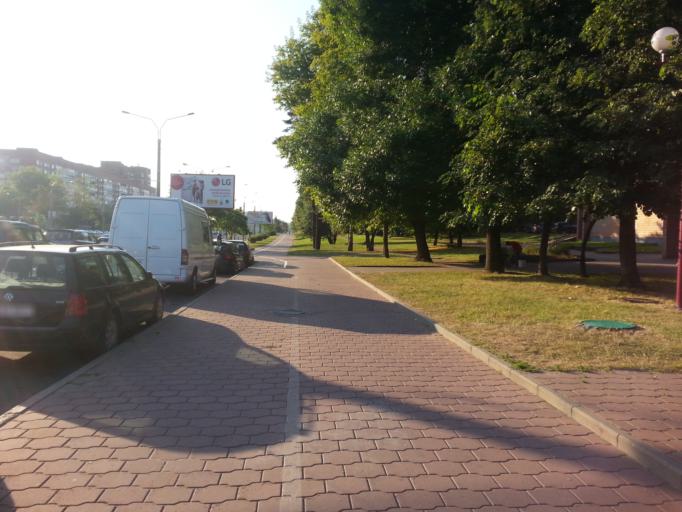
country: BY
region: Minsk
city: Vyaliki Trastsyanets
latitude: 53.8652
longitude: 27.6615
